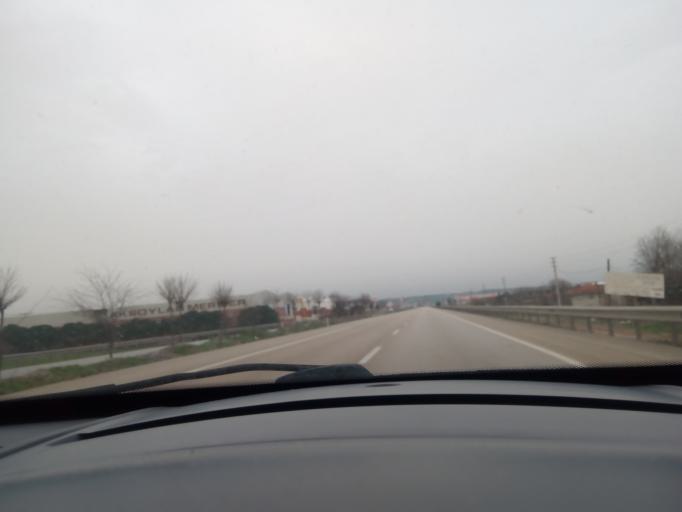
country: TR
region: Bursa
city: Tatkavakli
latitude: 40.0294
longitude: 28.3092
